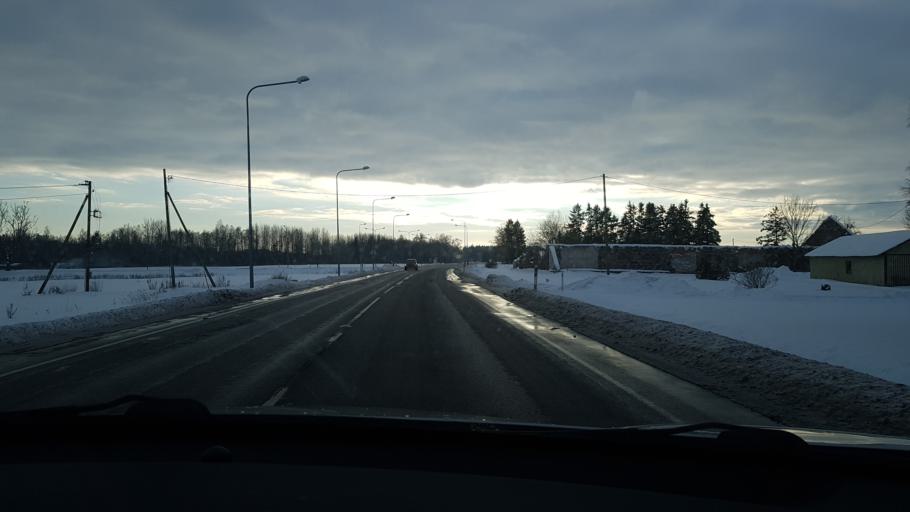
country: EE
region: Jaervamaa
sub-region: Paide linn
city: Paide
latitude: 58.9410
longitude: 25.6411
